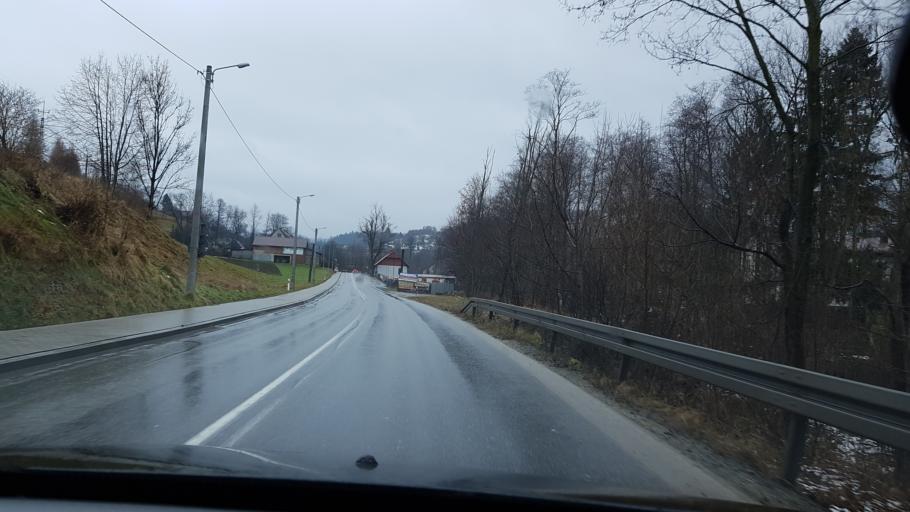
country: PL
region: Lesser Poland Voivodeship
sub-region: Powiat nowotarski
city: Raba Wyzna
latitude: 49.5610
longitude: 19.8785
